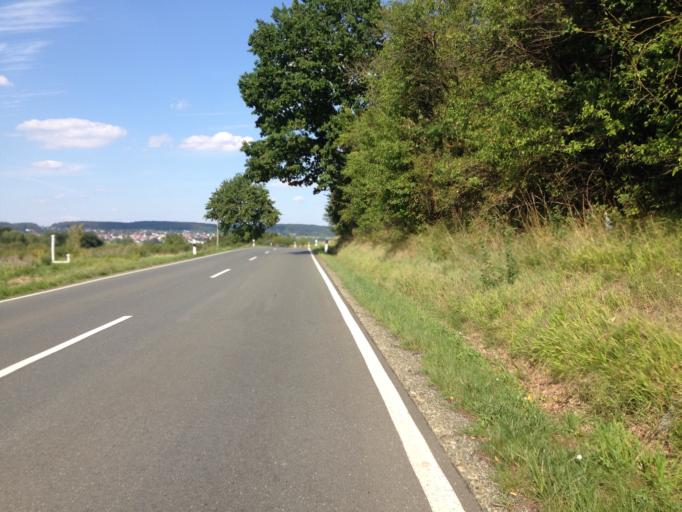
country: DE
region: Hesse
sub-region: Regierungsbezirk Giessen
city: Alten Buseck
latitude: 50.5980
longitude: 8.7393
